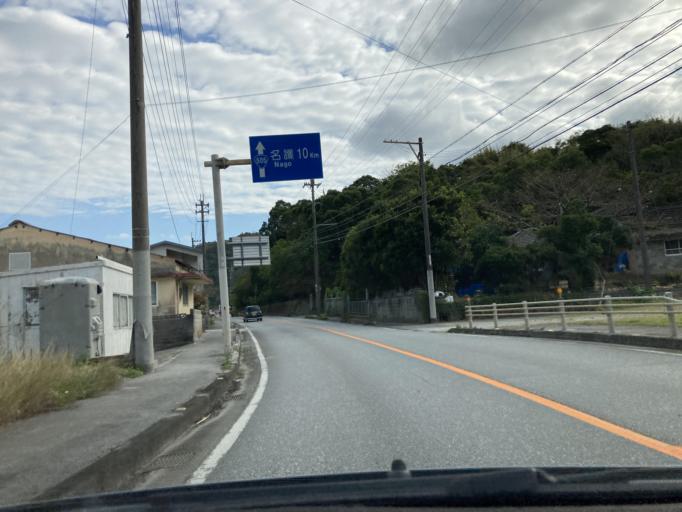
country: JP
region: Okinawa
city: Nago
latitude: 26.6528
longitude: 127.9809
